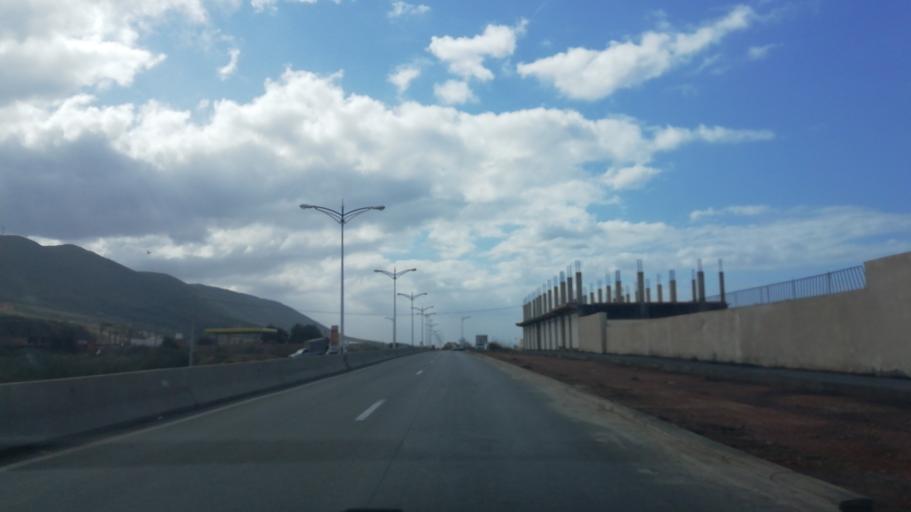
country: DZ
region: Mostaganem
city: Mostaganem
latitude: 36.0282
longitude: 0.1362
